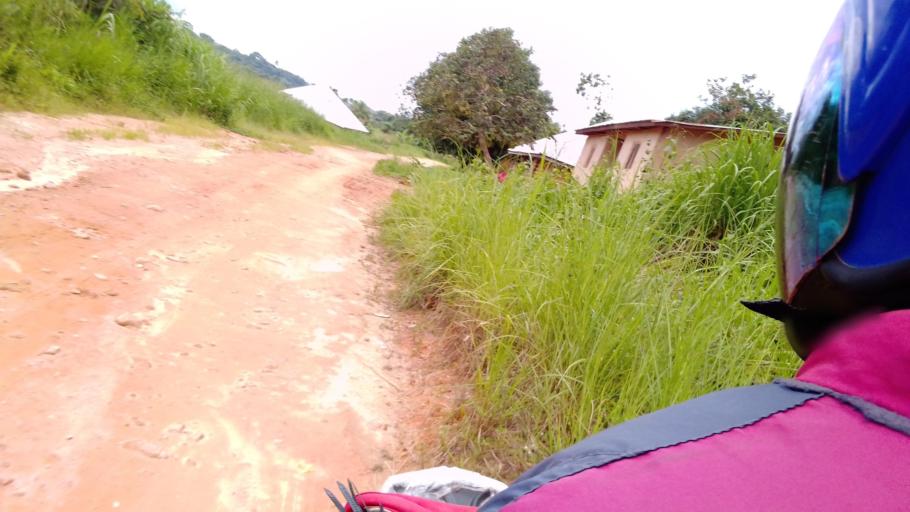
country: SL
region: Eastern Province
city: Koyima
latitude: 8.6931
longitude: -11.0103
